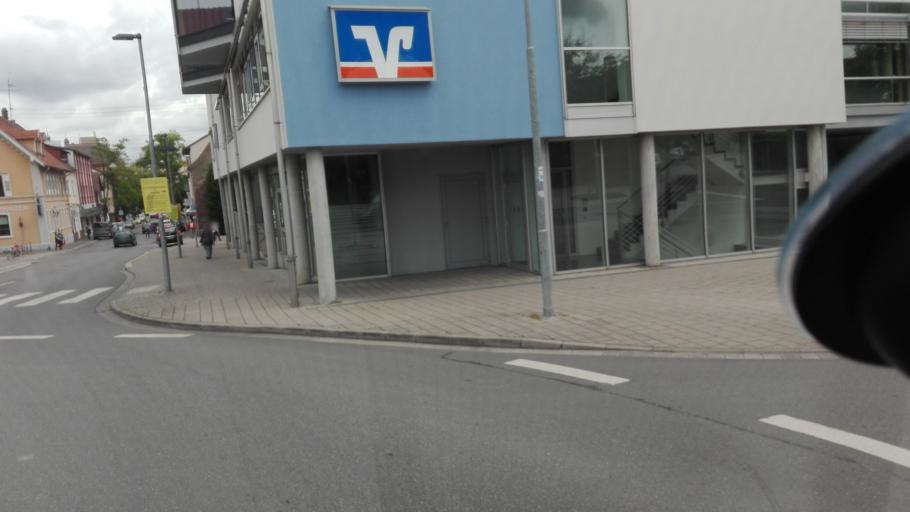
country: DE
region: Baden-Wuerttemberg
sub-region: Karlsruhe Region
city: Wiesloch
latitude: 49.2912
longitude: 8.6975
